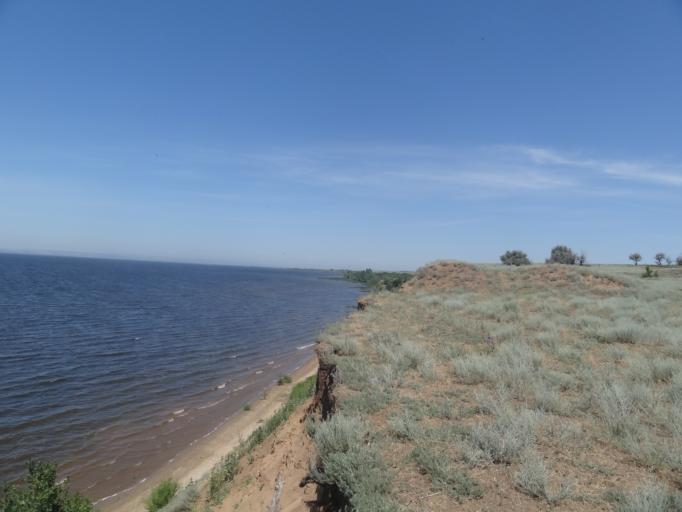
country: RU
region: Saratov
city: Krasnoarmeysk
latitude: 51.1007
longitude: 45.9357
